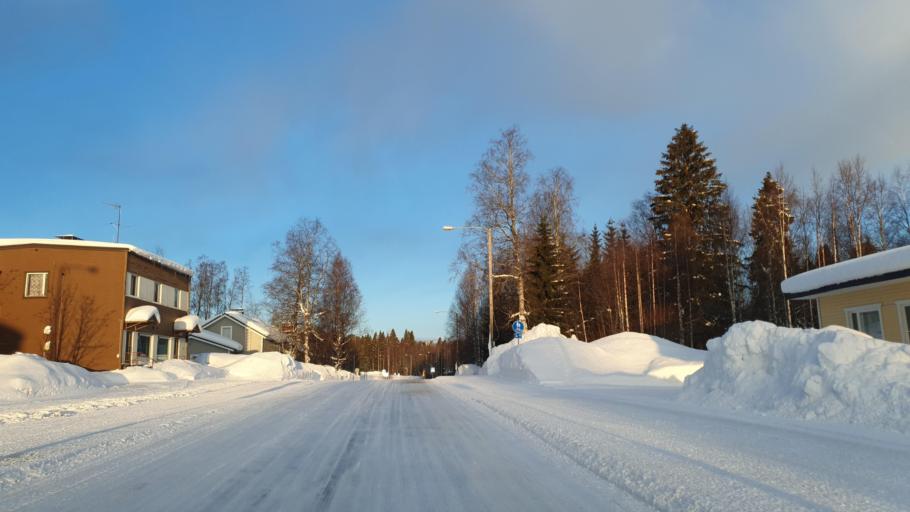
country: FI
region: Kainuu
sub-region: Kajaani
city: Ristijaervi
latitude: 64.3377
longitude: 28.1099
